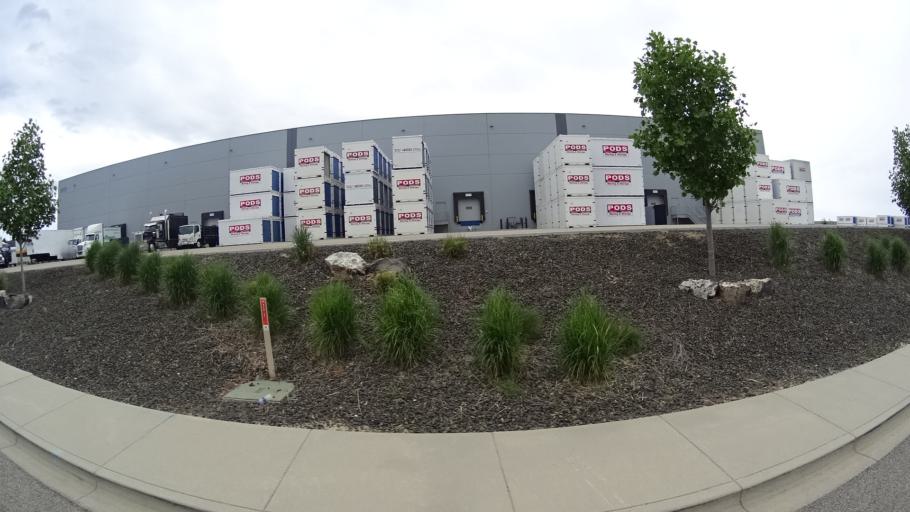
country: US
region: Idaho
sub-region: Ada County
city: Boise
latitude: 43.5403
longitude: -116.1653
